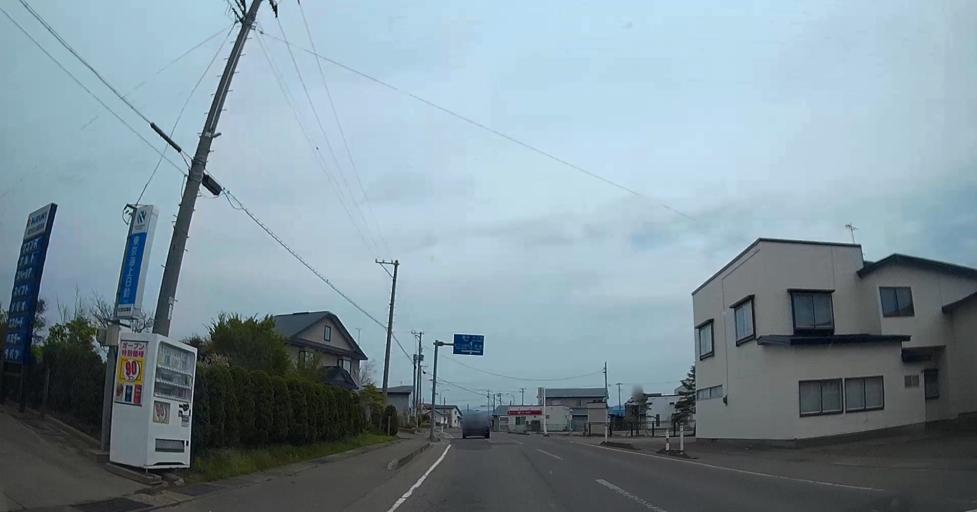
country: JP
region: Aomori
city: Shimokizukuri
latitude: 40.9777
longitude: 140.3726
